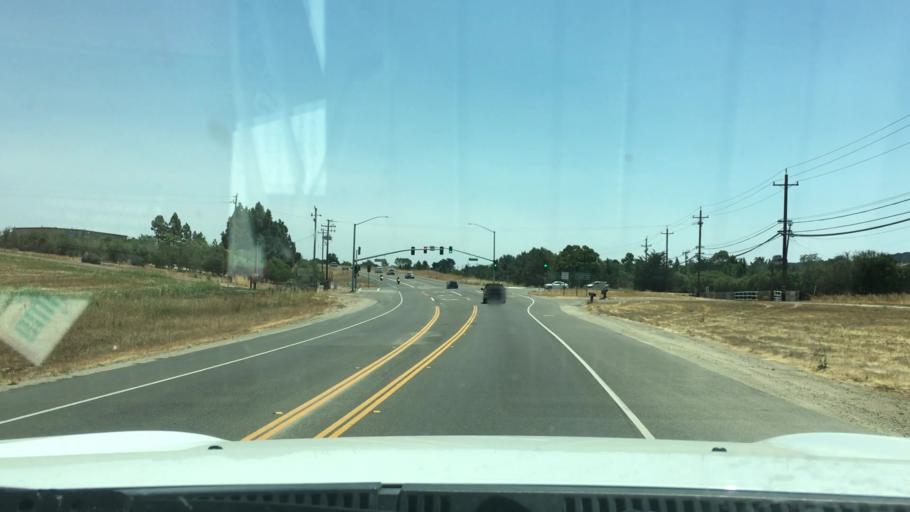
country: US
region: California
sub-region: San Luis Obispo County
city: San Luis Obispo
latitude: 35.2251
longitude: -120.6263
